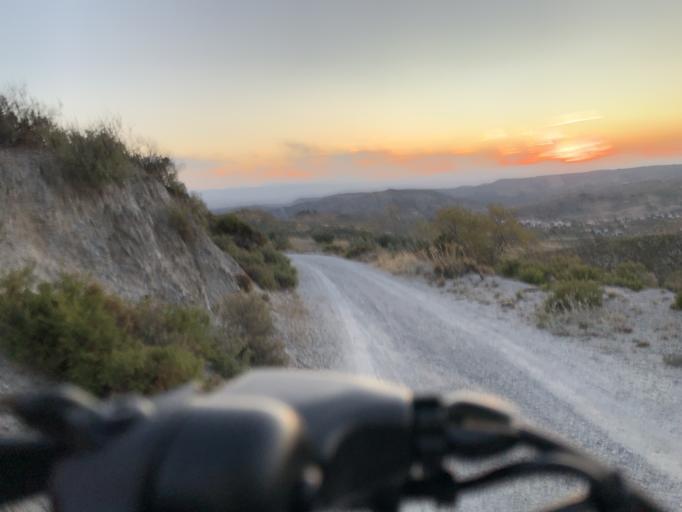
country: ES
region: Andalusia
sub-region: Provincia de Granada
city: Beas de Granada
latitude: 37.2233
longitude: -3.4592
